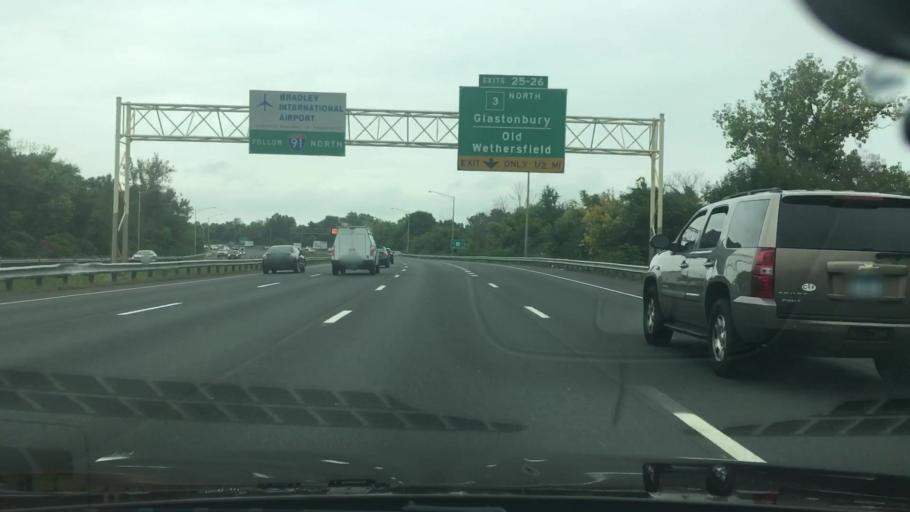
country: US
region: Connecticut
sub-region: Hartford County
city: Wethersfield
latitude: 41.6962
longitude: -72.6448
